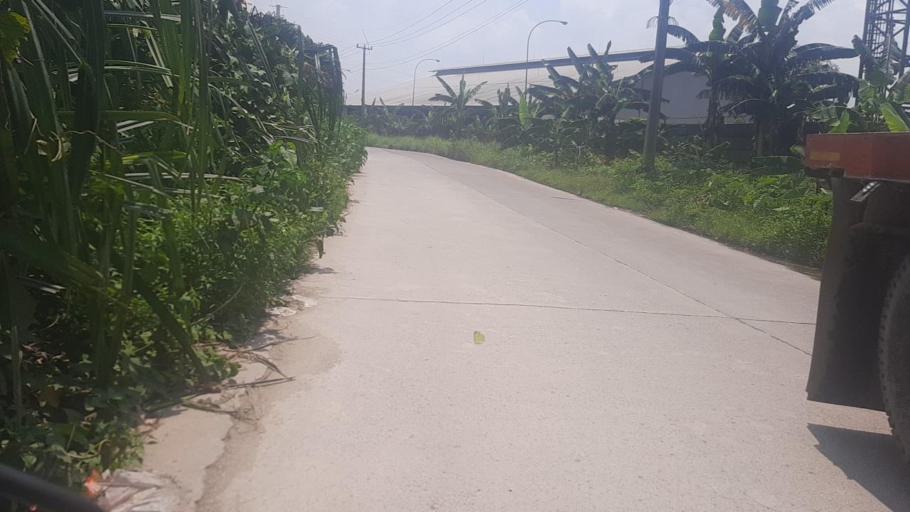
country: ID
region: West Java
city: Citeureup
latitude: -6.4605
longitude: 106.9297
